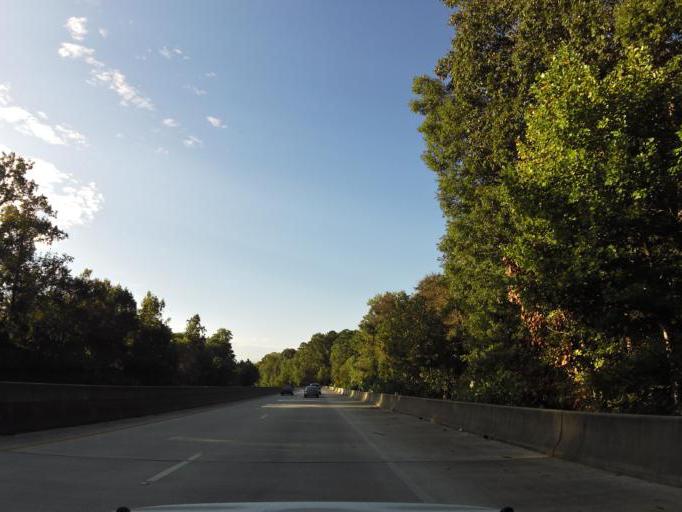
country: US
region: Georgia
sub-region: Cobb County
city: Powder Springs
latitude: 33.9190
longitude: -84.6289
